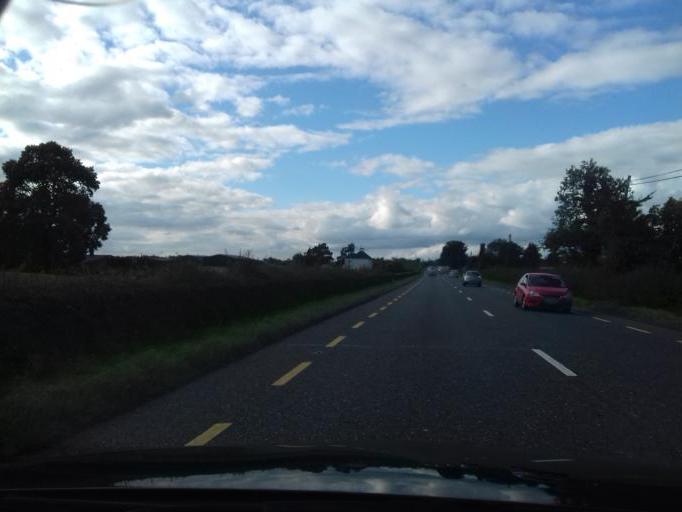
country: IE
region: Leinster
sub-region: Uibh Fhaili
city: Tullamore
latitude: 53.3096
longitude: -7.4993
